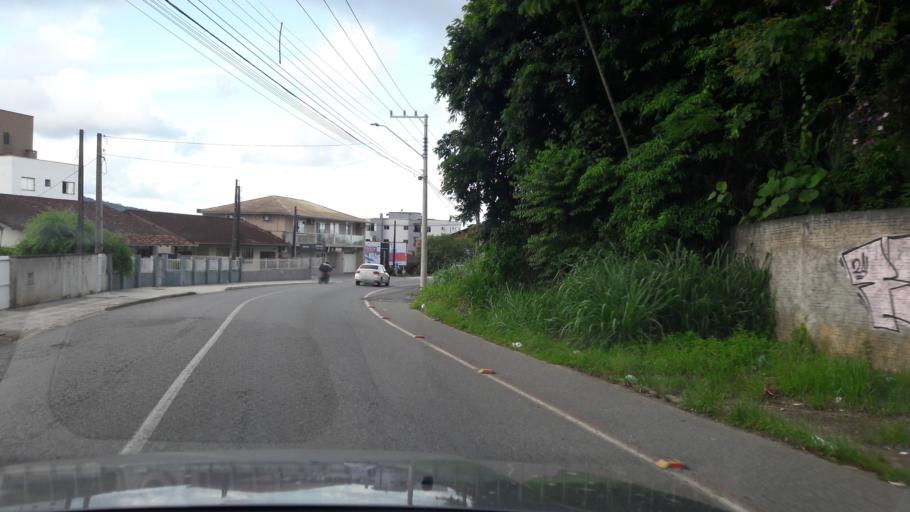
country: BR
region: Santa Catarina
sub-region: Joinville
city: Joinville
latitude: -26.3216
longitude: -48.8268
